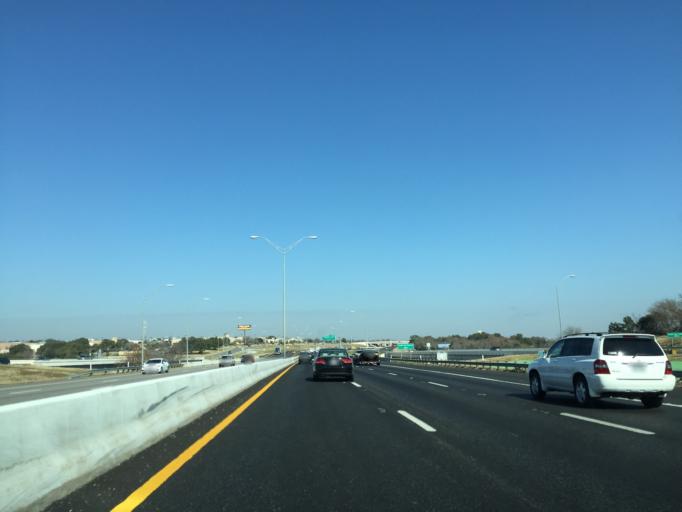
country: US
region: Texas
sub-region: Williamson County
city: Georgetown
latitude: 30.6243
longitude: -97.6906
